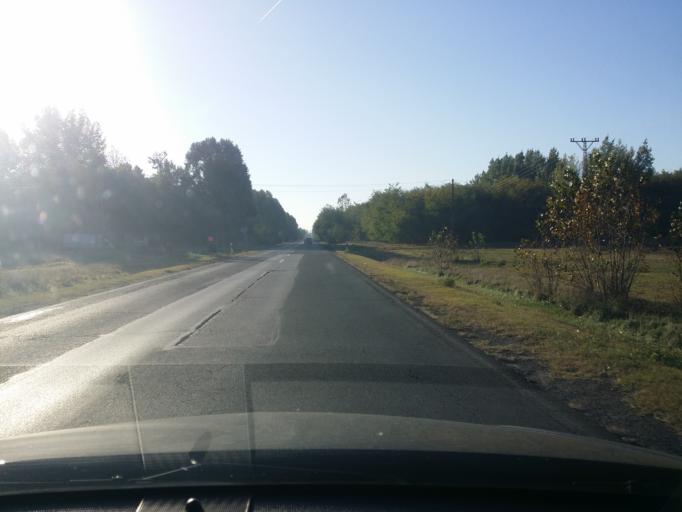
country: HU
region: Bacs-Kiskun
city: Nyarlorinc
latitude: 46.8778
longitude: 19.8470
